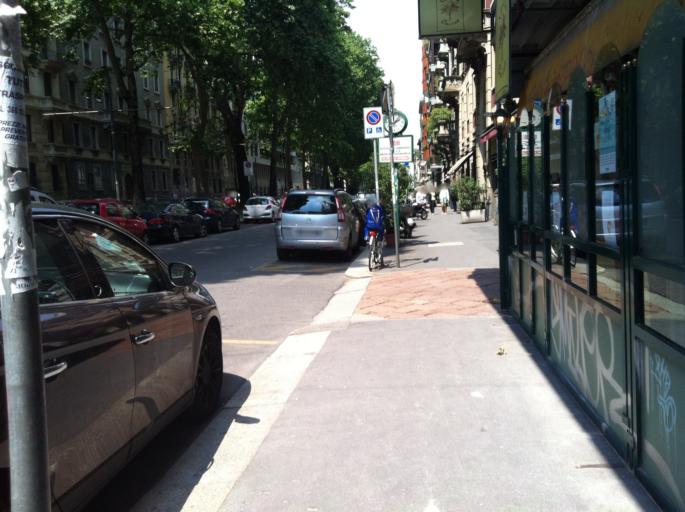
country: IT
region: Lombardy
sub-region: Citta metropolitana di Milano
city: Milano
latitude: 45.4655
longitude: 9.2073
